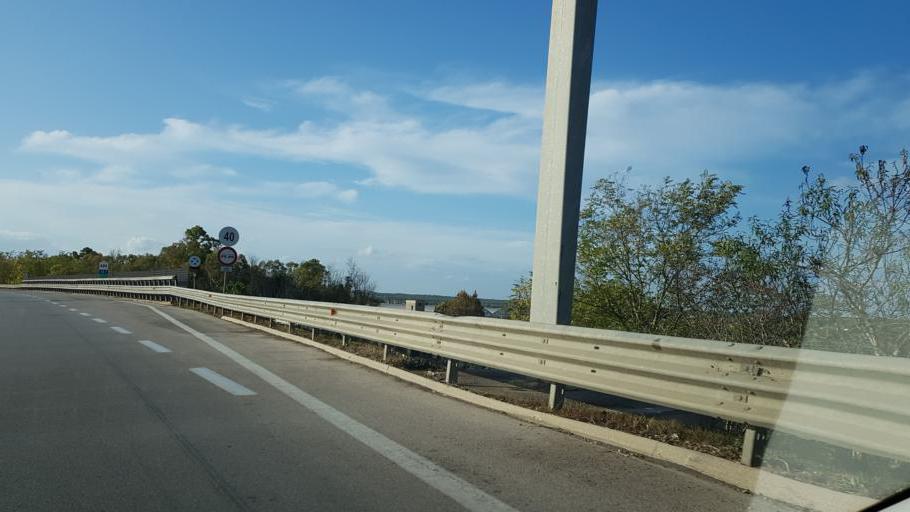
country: IT
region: Apulia
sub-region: Provincia di Brindisi
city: Francavilla Fontana
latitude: 40.5459
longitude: 17.5945
